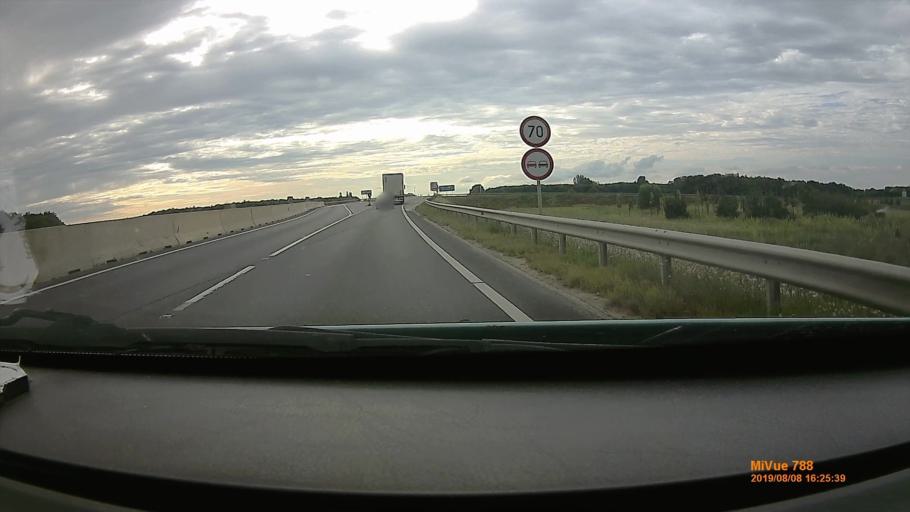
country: HU
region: Szabolcs-Szatmar-Bereg
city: Hodasz
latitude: 47.9698
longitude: 22.2116
